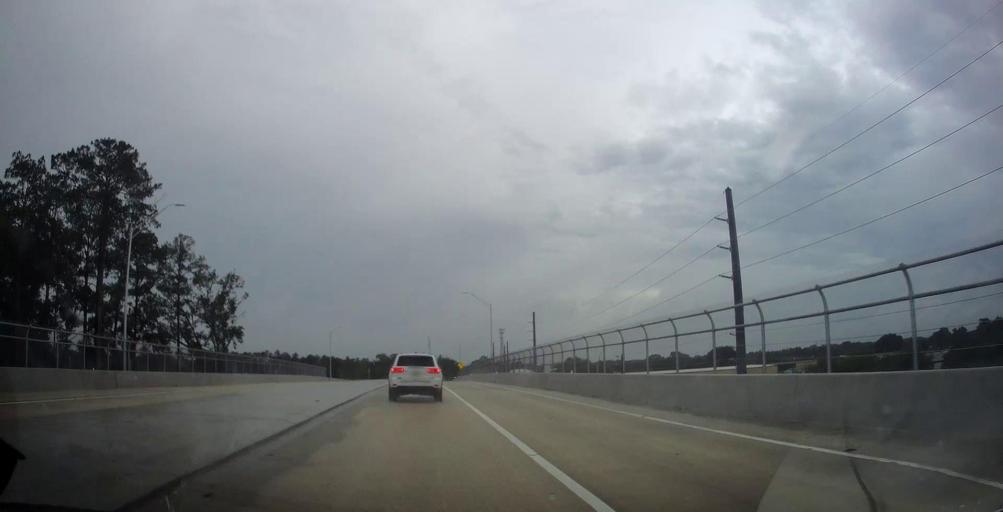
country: US
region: Florida
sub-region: Marion County
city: Ocala
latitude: 29.2106
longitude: -82.0866
